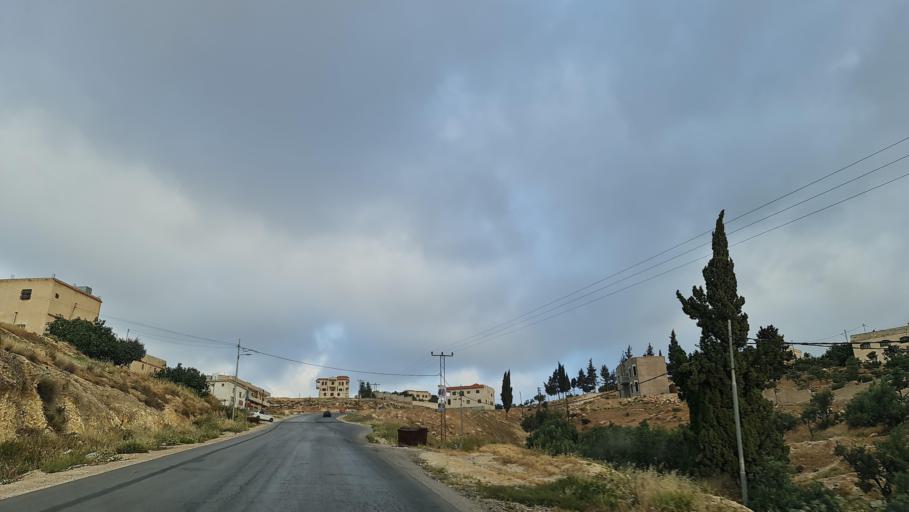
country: JO
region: Amman
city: Al Jubayhah
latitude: 32.0931
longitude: 35.9054
